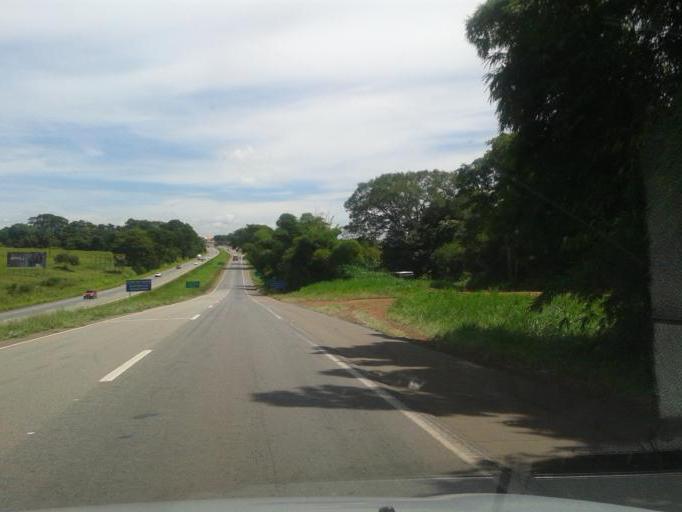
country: BR
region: Goias
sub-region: Hidrolandia
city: Hidrolandia
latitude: -16.9852
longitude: -49.2295
